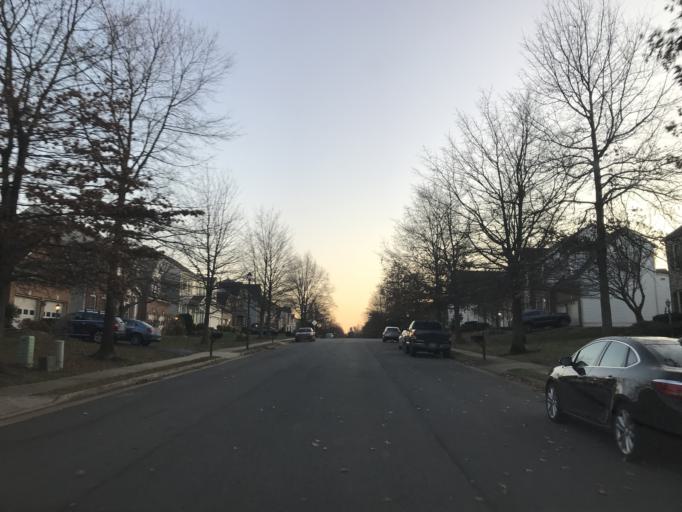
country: US
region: Virginia
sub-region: Fairfax County
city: Franconia
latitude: 38.7858
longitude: -77.1570
